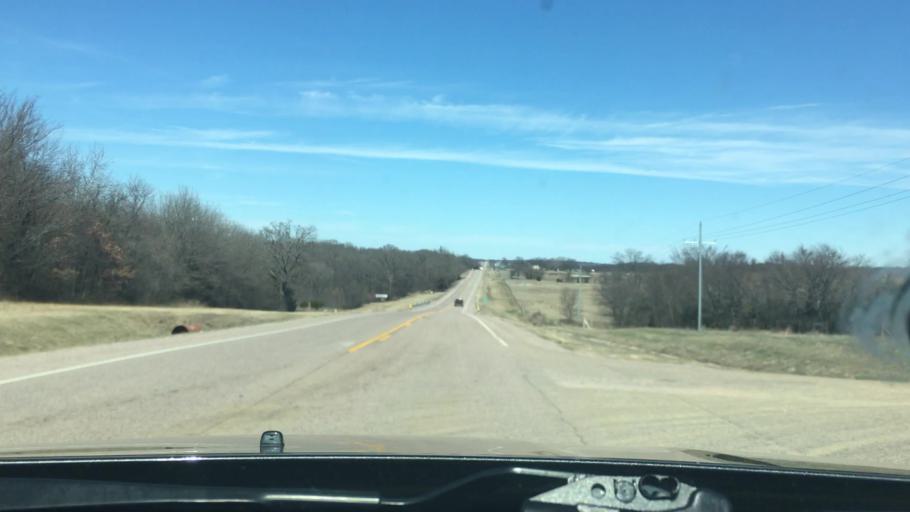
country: US
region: Oklahoma
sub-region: Murray County
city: Sulphur
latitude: 34.4074
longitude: -96.9507
